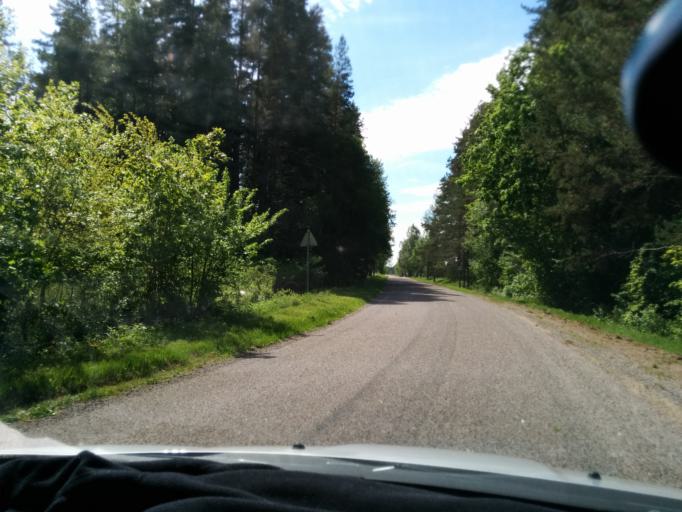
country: EE
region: Harju
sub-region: Loksa linn
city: Loksa
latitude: 59.5206
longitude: 25.9492
